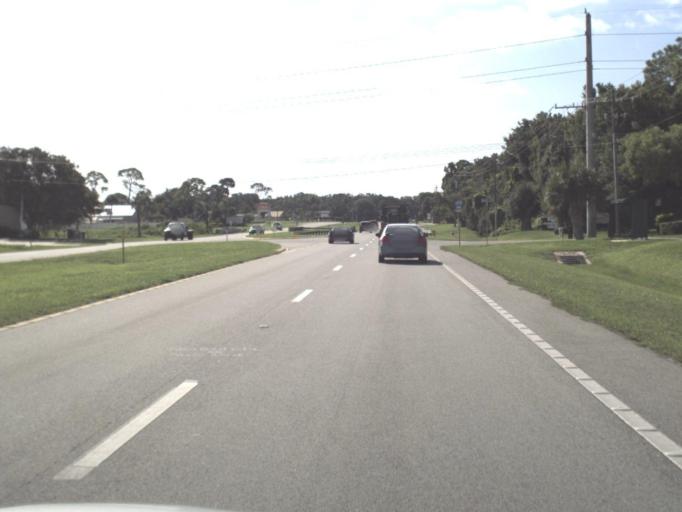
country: US
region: Florida
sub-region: Sarasota County
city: Vamo
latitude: 27.2227
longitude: -82.4921
